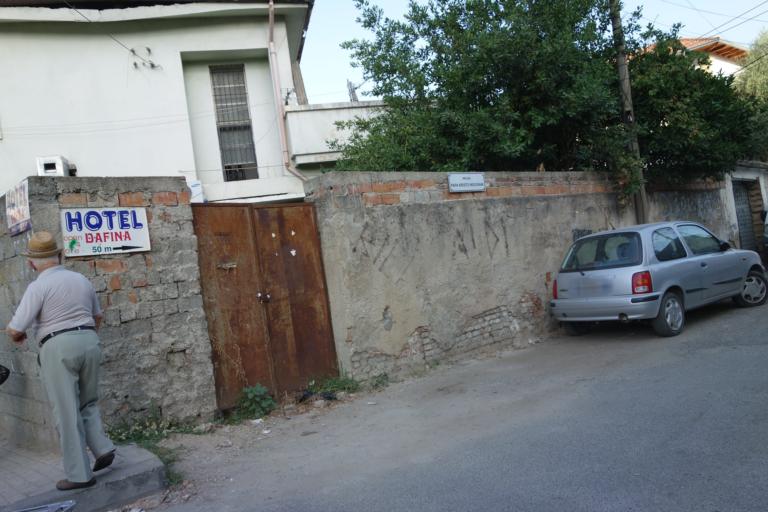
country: AL
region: Tirane
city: Tirana
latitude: 41.3335
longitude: 19.8180
